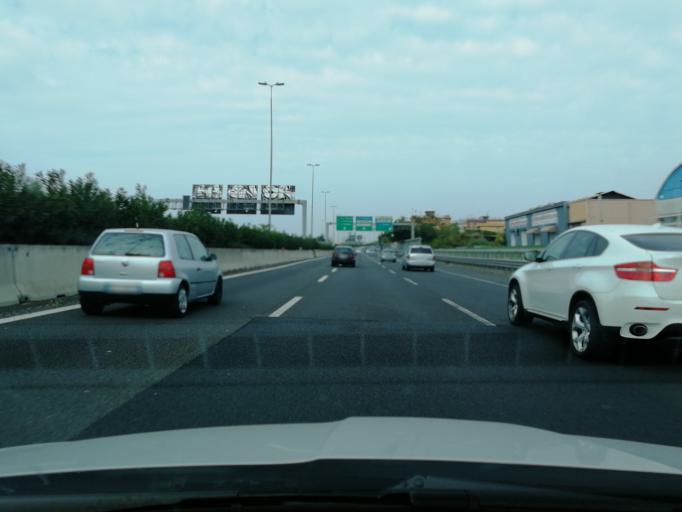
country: IT
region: Latium
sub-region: Citta metropolitana di Roma Capitale
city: Ciampino
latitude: 41.8594
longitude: 12.5994
